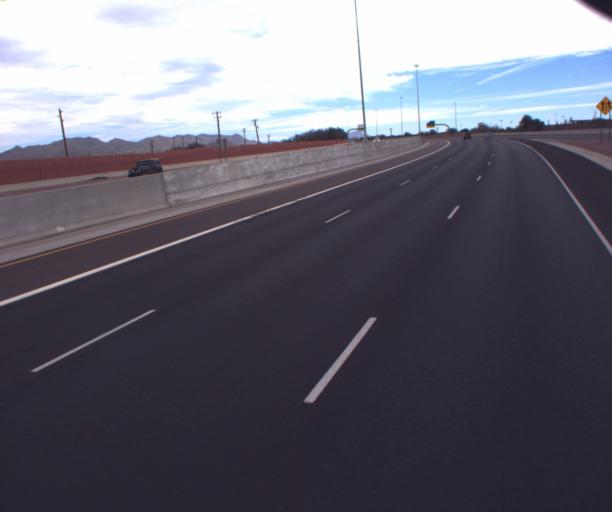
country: US
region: Arizona
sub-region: Maricopa County
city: Mesa
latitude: 33.4813
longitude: -111.7504
